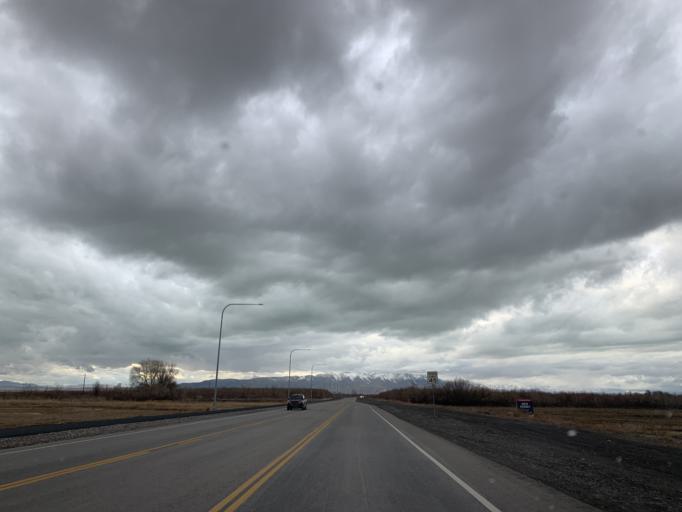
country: US
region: Utah
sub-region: Utah County
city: Provo
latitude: 40.2105
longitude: -111.6785
